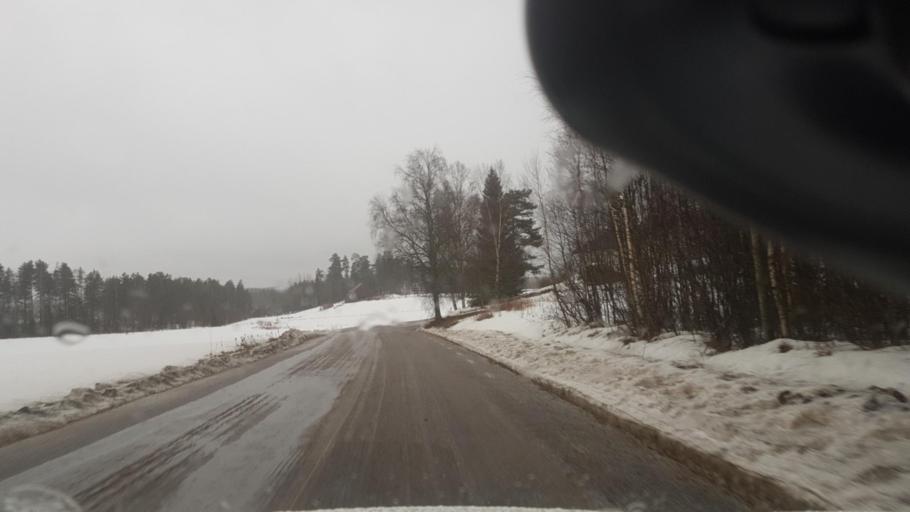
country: SE
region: Vaermland
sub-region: Eda Kommun
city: Charlottenberg
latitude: 59.8661
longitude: 12.3455
